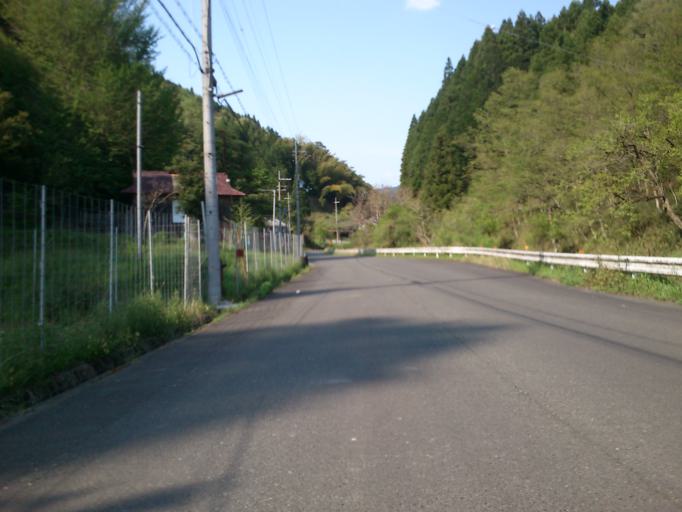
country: JP
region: Kyoto
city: Fukuchiyama
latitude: 35.3463
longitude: 135.0081
